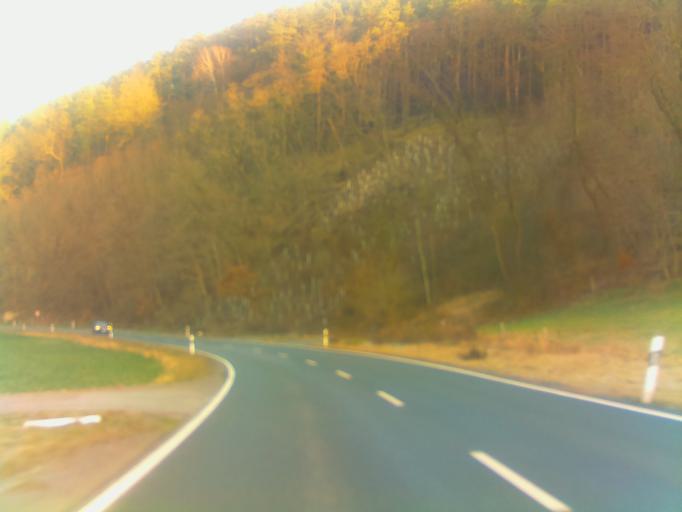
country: DE
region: Thuringia
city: Freienorla
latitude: 50.7608
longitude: 11.5454
